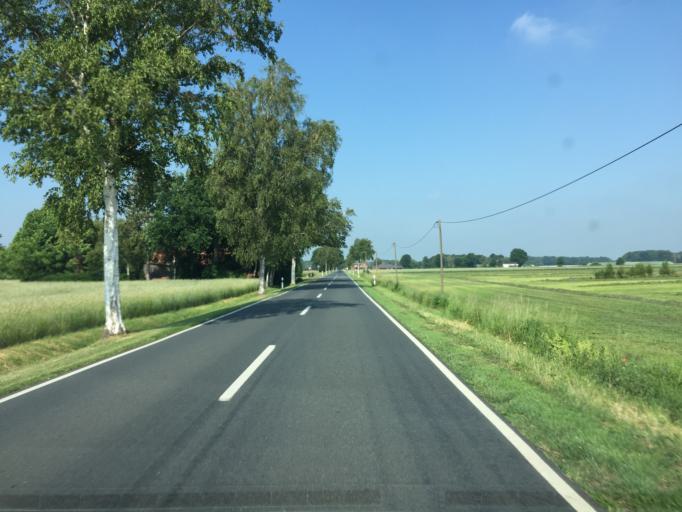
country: DE
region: Lower Saxony
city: Bahrenborstel
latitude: 52.5364
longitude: 8.7324
